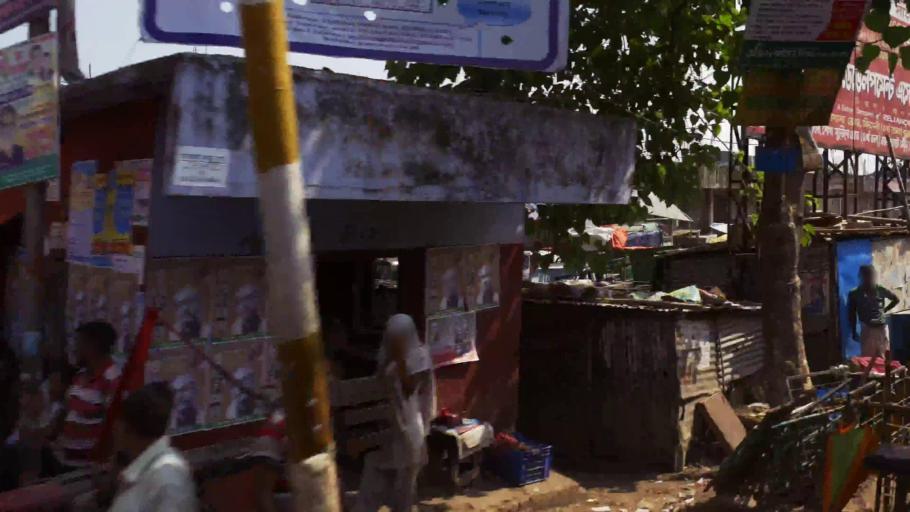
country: BD
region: Dhaka
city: Tungi
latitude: 23.8850
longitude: 90.4068
